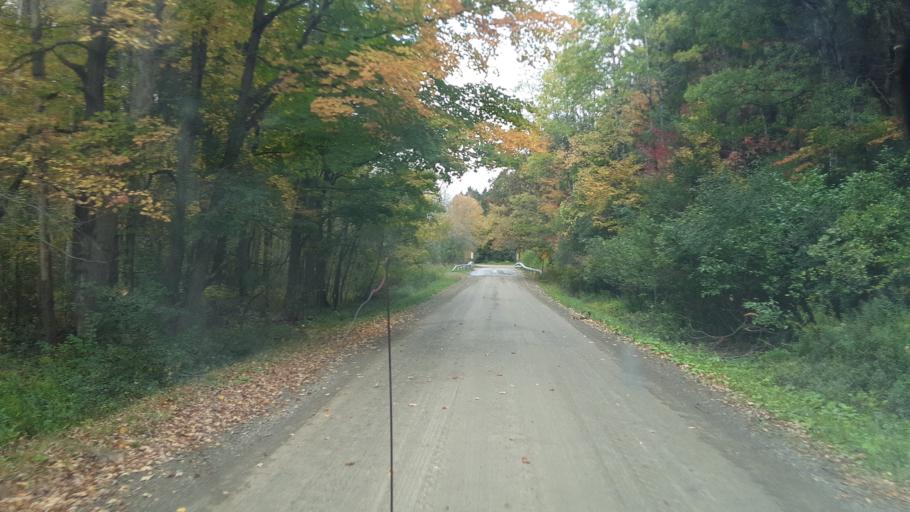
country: US
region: New York
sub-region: Allegany County
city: Alfred
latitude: 42.3688
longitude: -77.8461
